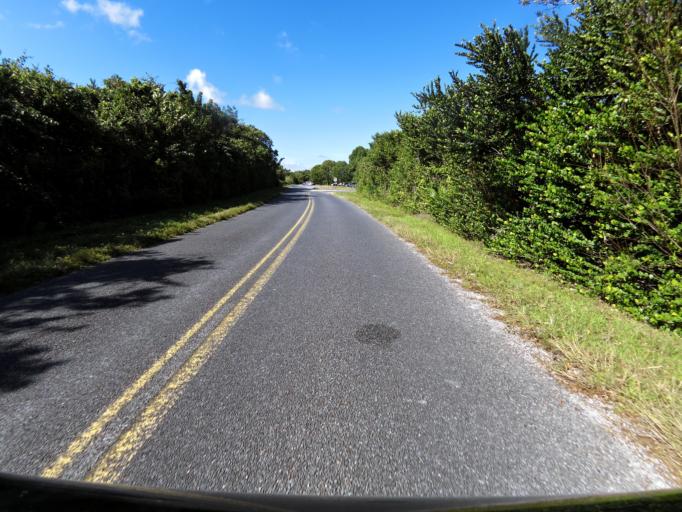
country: US
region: Florida
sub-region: Miami-Dade County
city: Florida City
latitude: 25.4396
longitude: -80.7823
